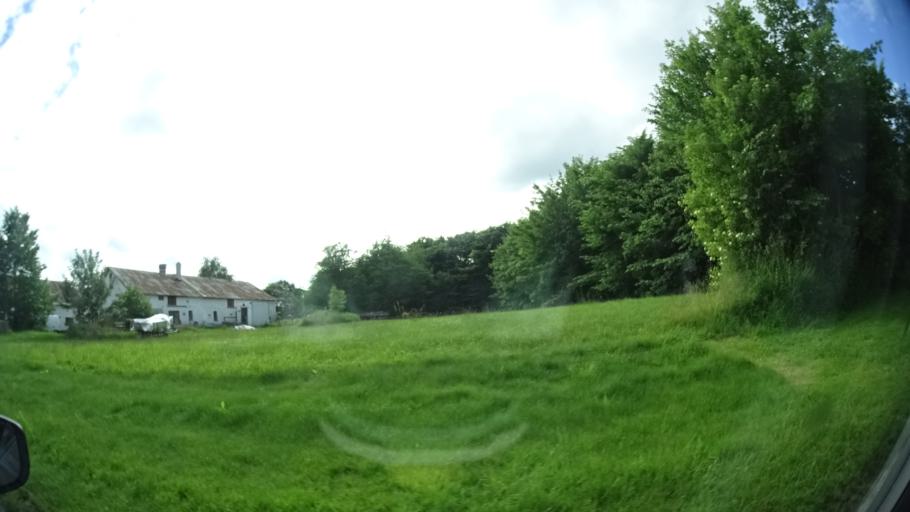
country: DK
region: Central Jutland
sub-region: Norddjurs Kommune
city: Grenaa
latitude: 56.4699
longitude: 10.7155
